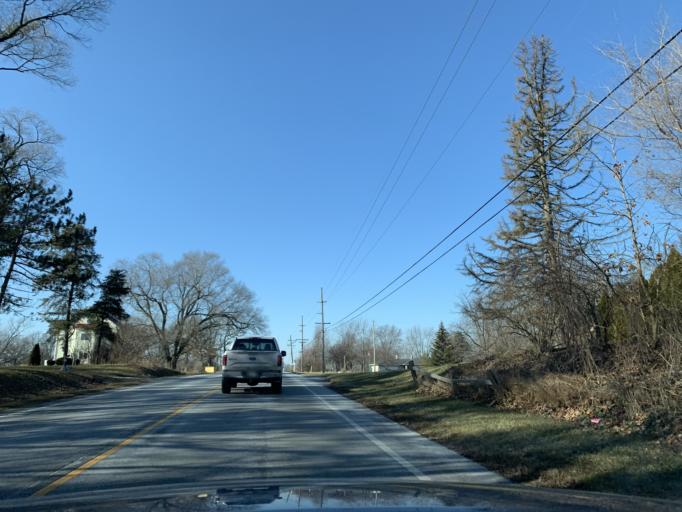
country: US
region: Indiana
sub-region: Lake County
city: Crown Point
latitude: 41.4207
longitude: -87.3989
